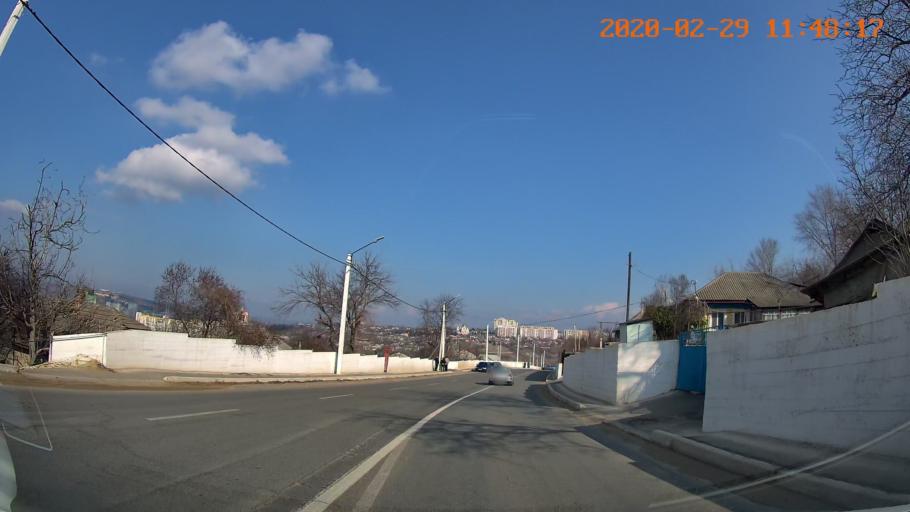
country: MD
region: Rezina
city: Rezina
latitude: 47.7473
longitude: 28.9896
